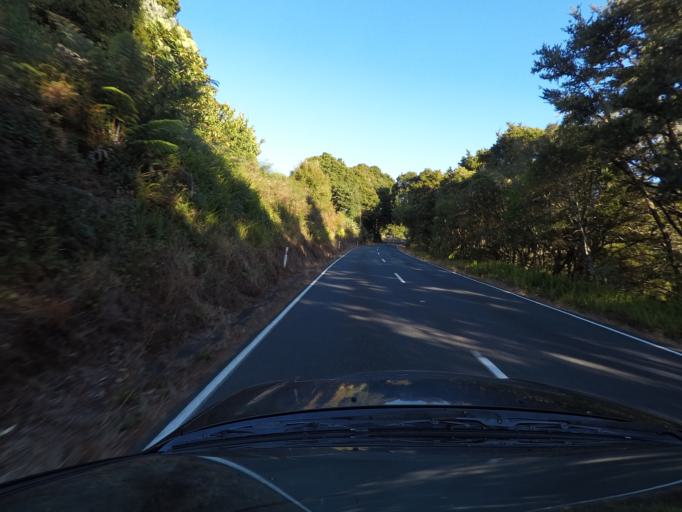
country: NZ
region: Northland
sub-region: Whangarei
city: Whangarei
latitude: -35.6637
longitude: 174.3181
